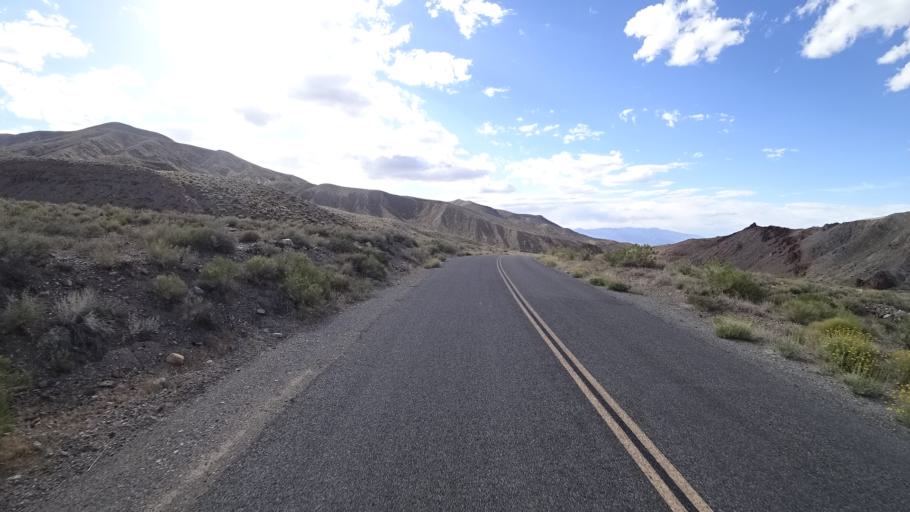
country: US
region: Nevada
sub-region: Nye County
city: Beatty
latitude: 36.4154
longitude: -117.1852
